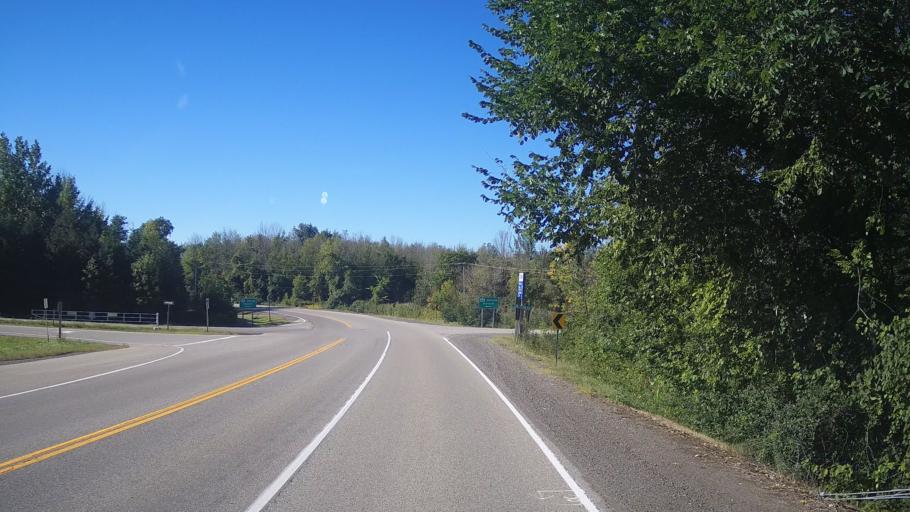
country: CA
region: Ontario
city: Bells Corners
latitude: 45.0787
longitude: -75.6338
